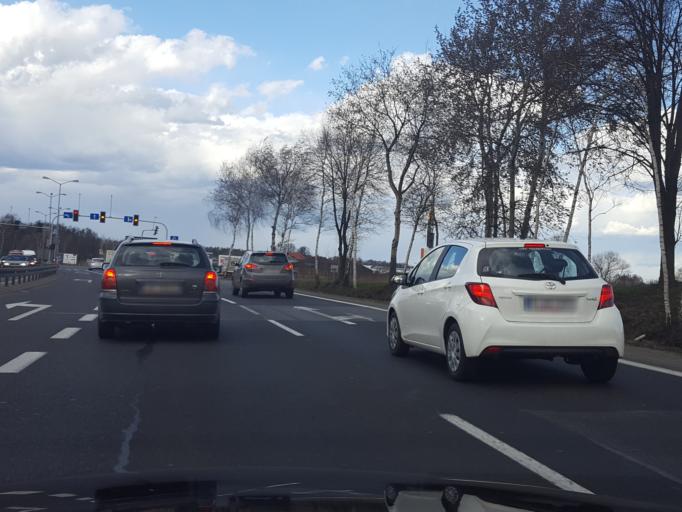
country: PL
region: Silesian Voivodeship
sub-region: Powiat pszczynski
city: Piasek
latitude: 50.0102
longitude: 18.9576
